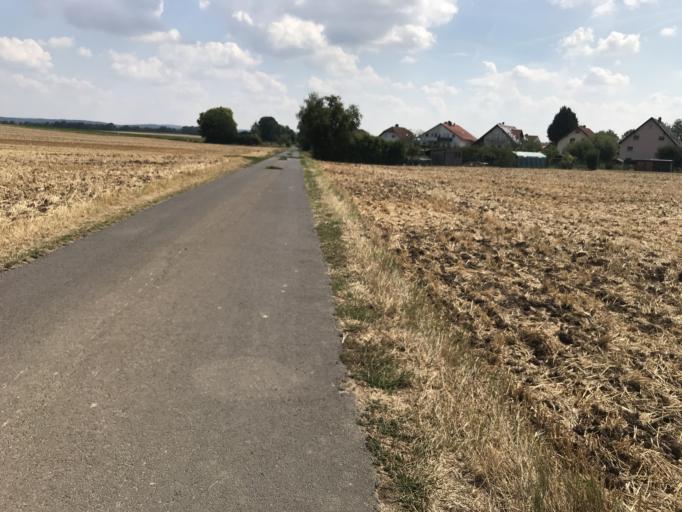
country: DE
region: Hesse
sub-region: Regierungsbezirk Darmstadt
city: Wolfersheim
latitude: 50.4428
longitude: 8.8390
